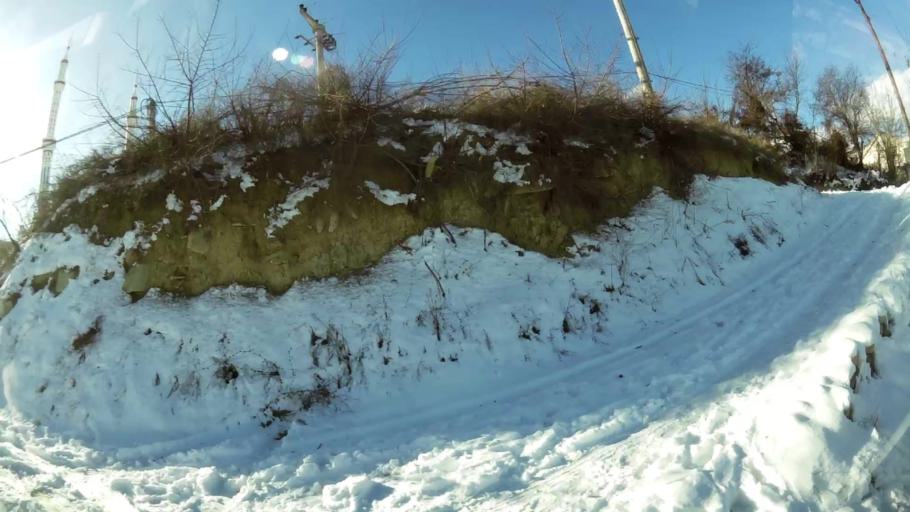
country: MK
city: Ljubin
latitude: 41.9797
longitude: 21.3034
